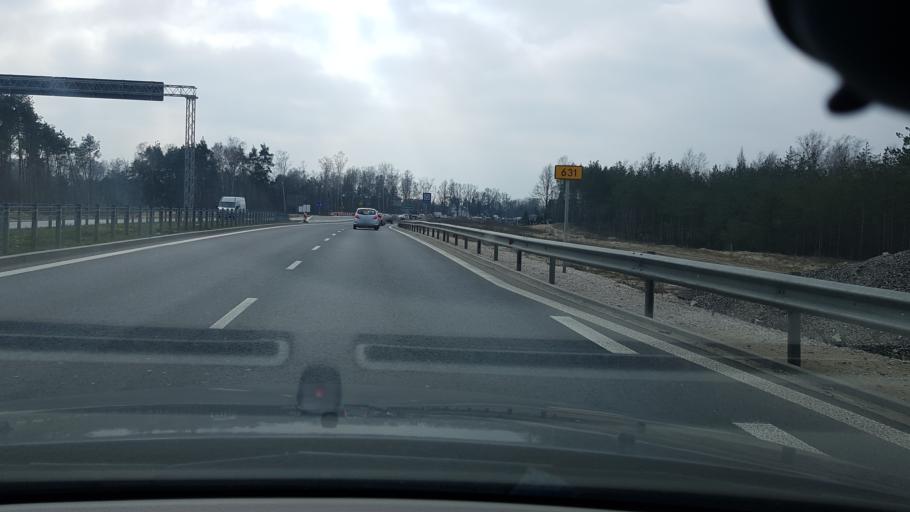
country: PL
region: Masovian Voivodeship
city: Zielonka
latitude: 52.3207
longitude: 21.1456
